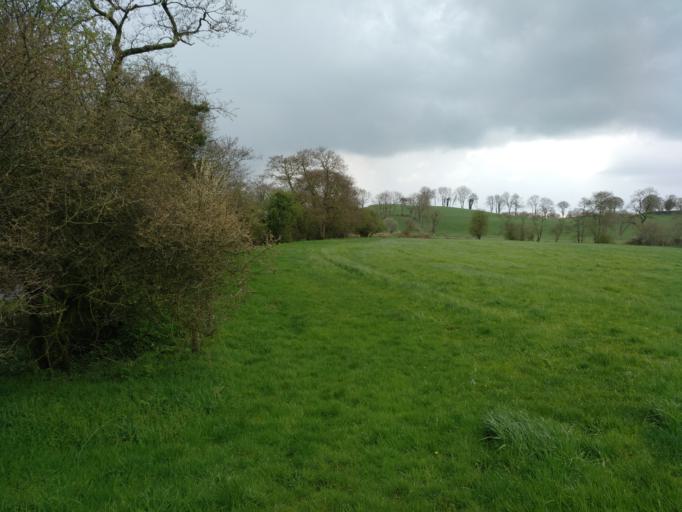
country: IE
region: Ulster
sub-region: County Monaghan
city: Clones
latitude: 54.1912
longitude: -7.1530
